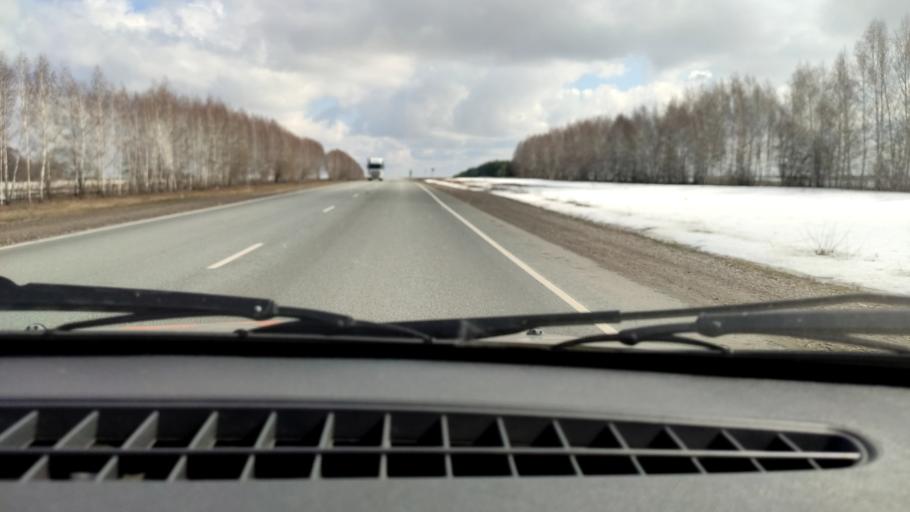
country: RU
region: Bashkortostan
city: Kudeyevskiy
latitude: 54.8090
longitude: 56.6429
